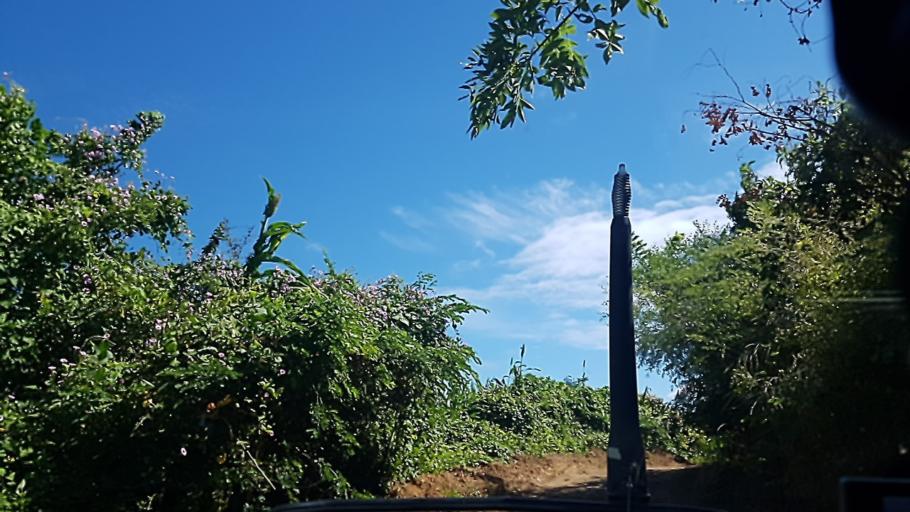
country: NI
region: Granada
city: Nandaime
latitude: 11.5713
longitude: -86.0903
